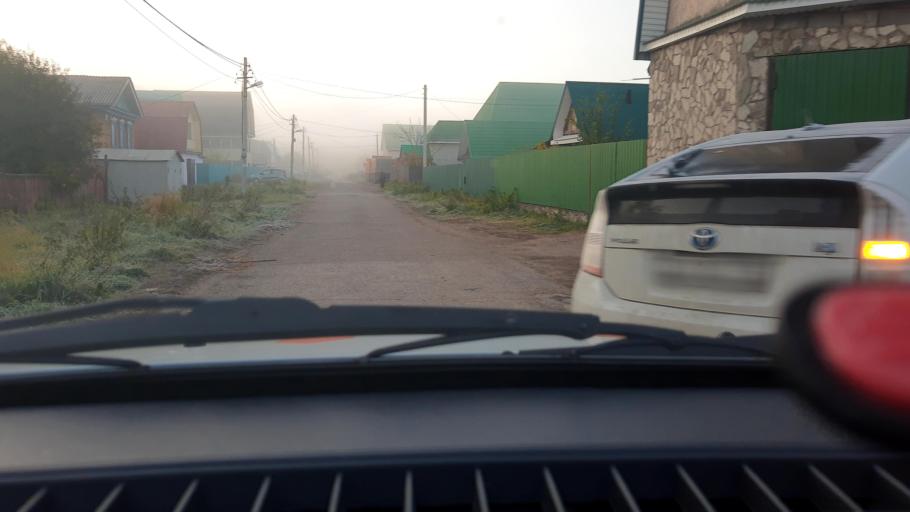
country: RU
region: Bashkortostan
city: Ufa
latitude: 54.7311
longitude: 55.9041
